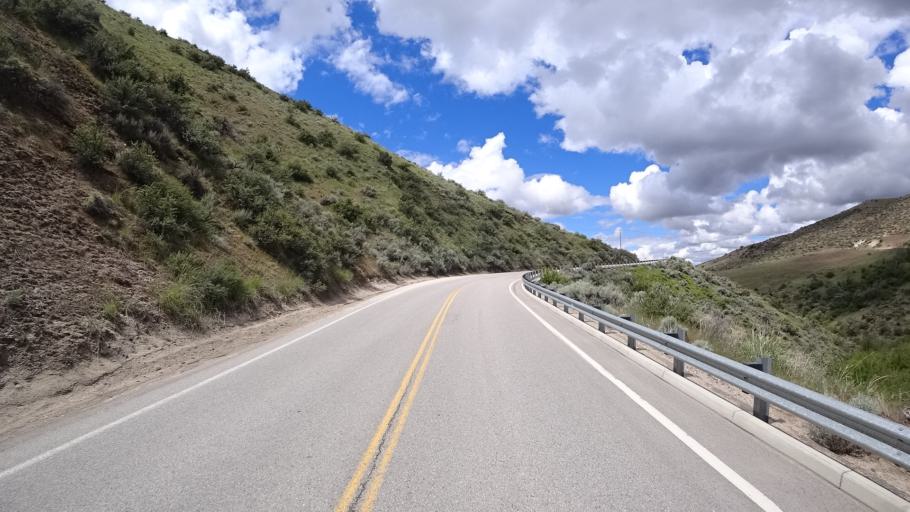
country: US
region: Idaho
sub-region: Ada County
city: Boise
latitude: 43.6869
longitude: -116.1808
